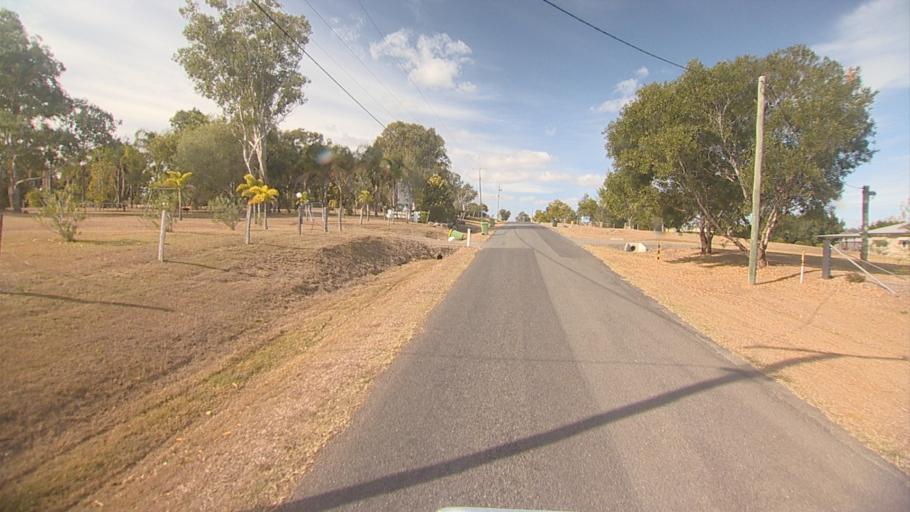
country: AU
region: Queensland
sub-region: Logan
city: Cedar Vale
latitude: -27.9153
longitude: 152.9920
